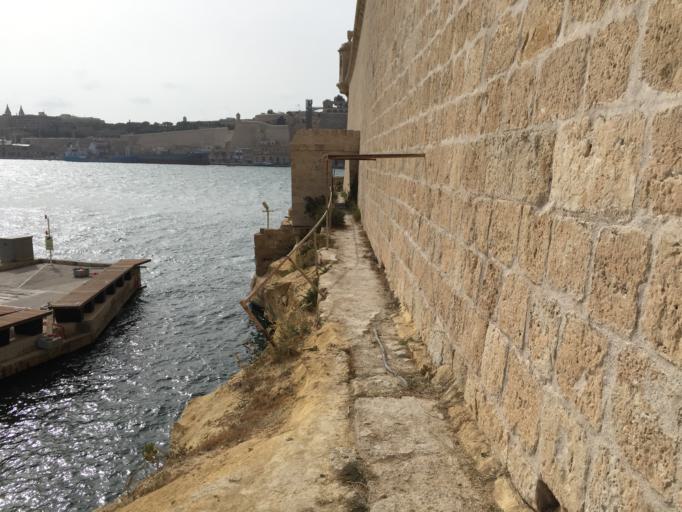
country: MT
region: Il-Birgu
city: Vittoriosa
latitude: 35.8919
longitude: 14.5176
